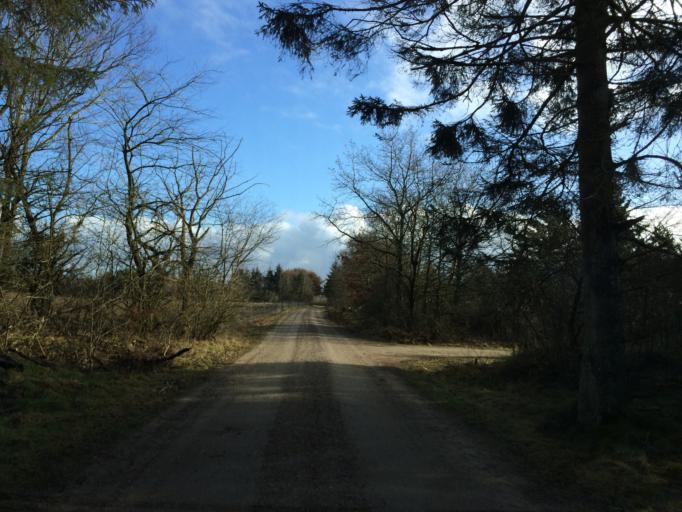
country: DK
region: Central Jutland
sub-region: Holstebro Kommune
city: Ulfborg
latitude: 56.2783
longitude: 8.3594
